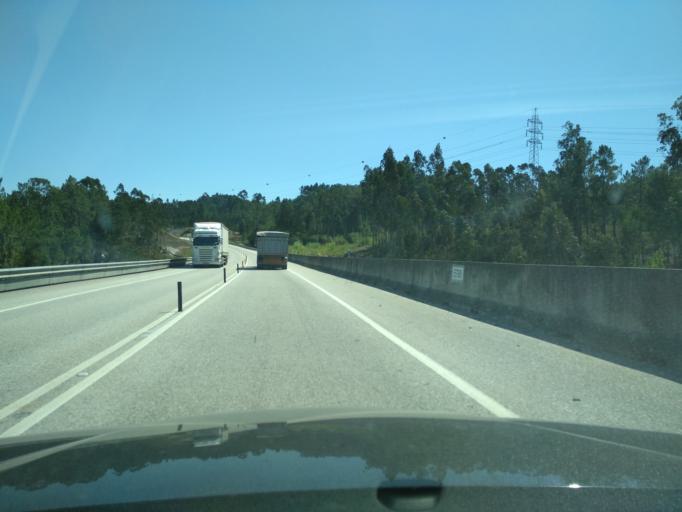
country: PT
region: Leiria
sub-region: Pombal
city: Lourical
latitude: 39.9587
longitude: -8.6924
